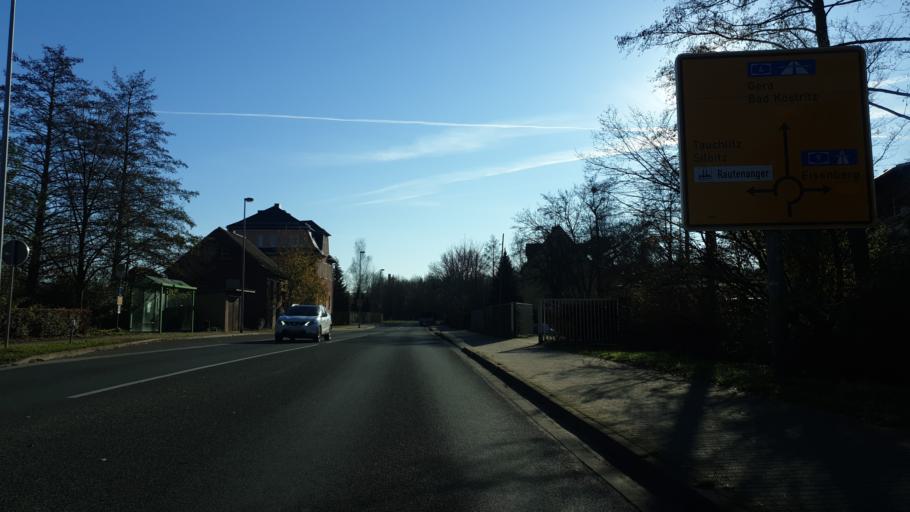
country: DE
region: Thuringia
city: Hartmannsdorf
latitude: 50.9656
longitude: 11.9833
